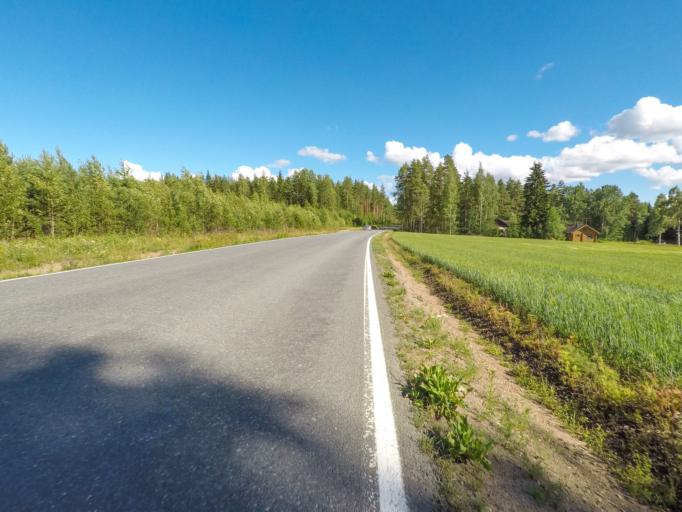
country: FI
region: South Karelia
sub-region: Lappeenranta
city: Taipalsaari
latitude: 61.1789
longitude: 28.0077
